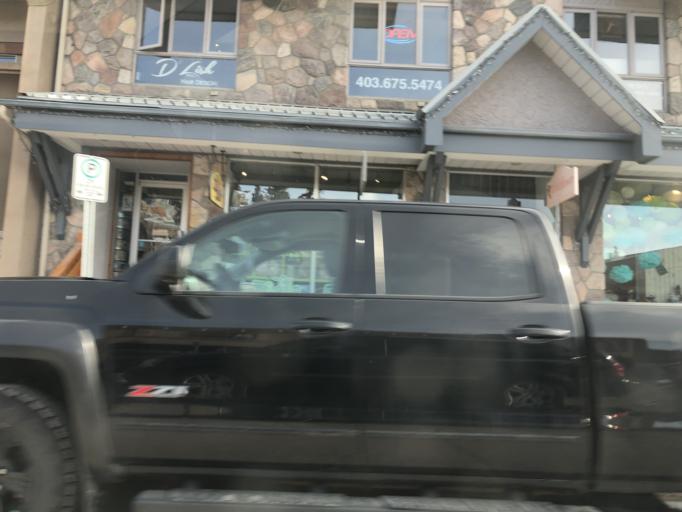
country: CA
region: Alberta
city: Canmore
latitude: 51.0892
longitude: -115.3593
